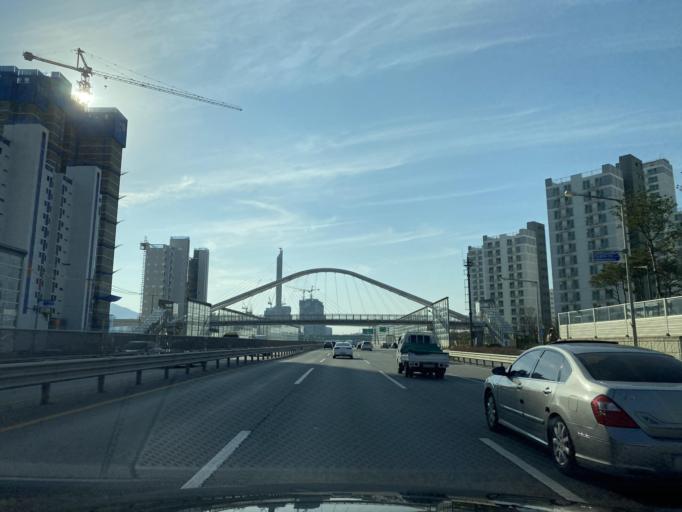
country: KR
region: Chungcheongnam-do
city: Cheonan
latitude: 36.7801
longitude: 127.0882
